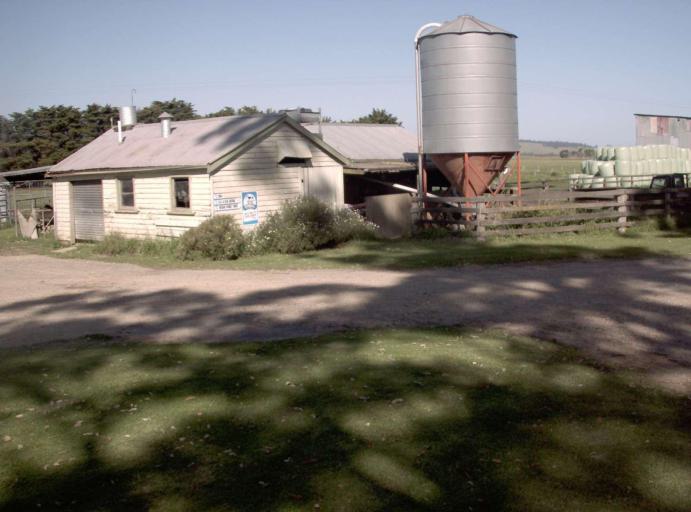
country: AU
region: Victoria
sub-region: East Gippsland
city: Lakes Entrance
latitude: -37.7432
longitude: 148.5134
